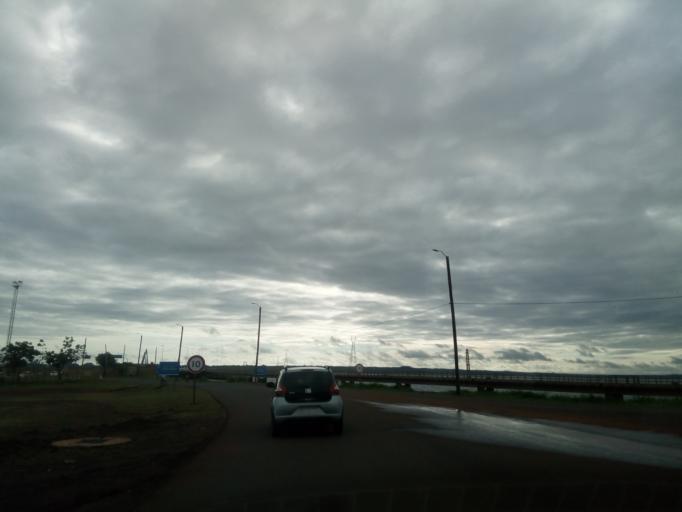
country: AR
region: Misiones
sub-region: Departamento de Capital
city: Posadas
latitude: -27.3771
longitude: -55.8827
